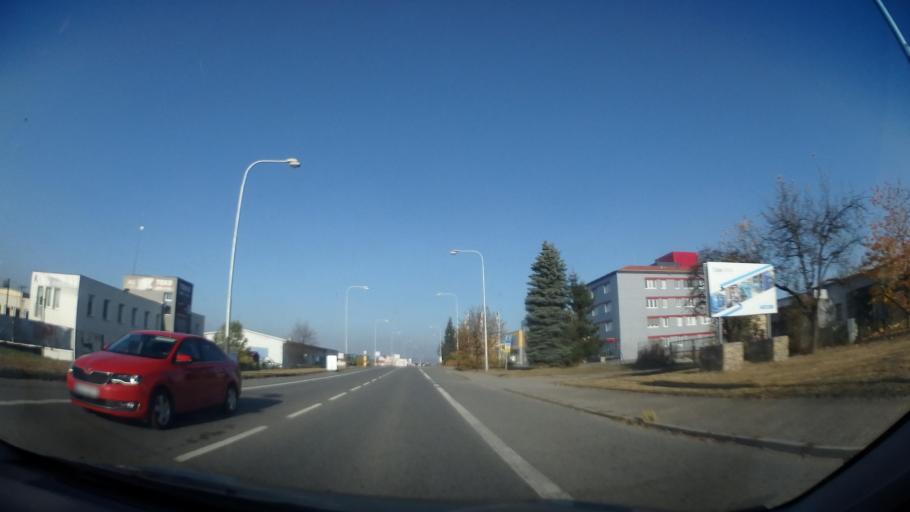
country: CZ
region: Vysocina
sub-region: Okres Zd'ar nad Sazavou
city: Zd'ar nad Sazavou
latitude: 49.5524
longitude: 15.9535
